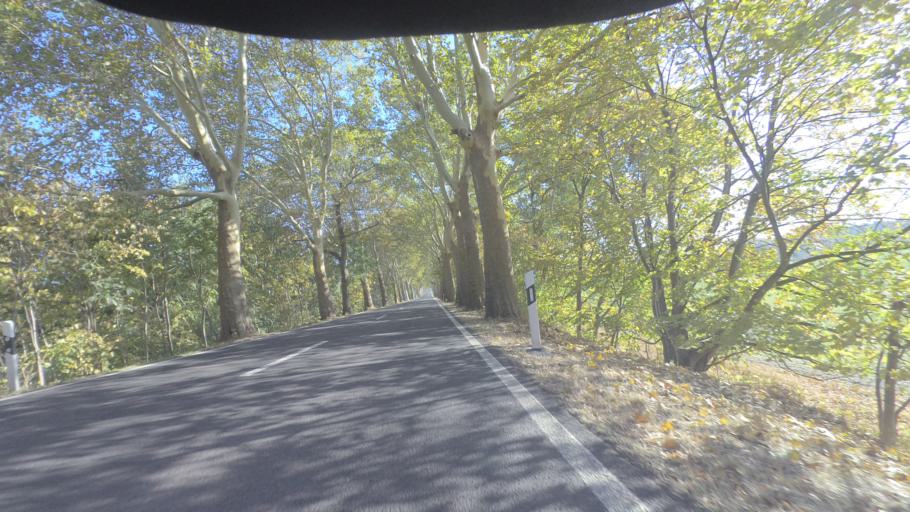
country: DE
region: Brandenburg
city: Zossen
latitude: 52.2497
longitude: 13.4841
